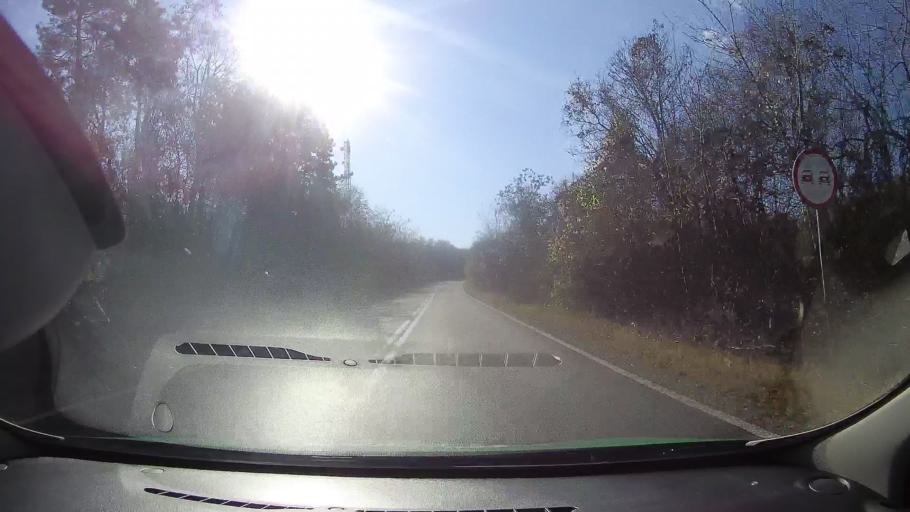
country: RO
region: Tulcea
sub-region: Oras Babadag
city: Babadag
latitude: 44.8336
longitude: 28.6948
